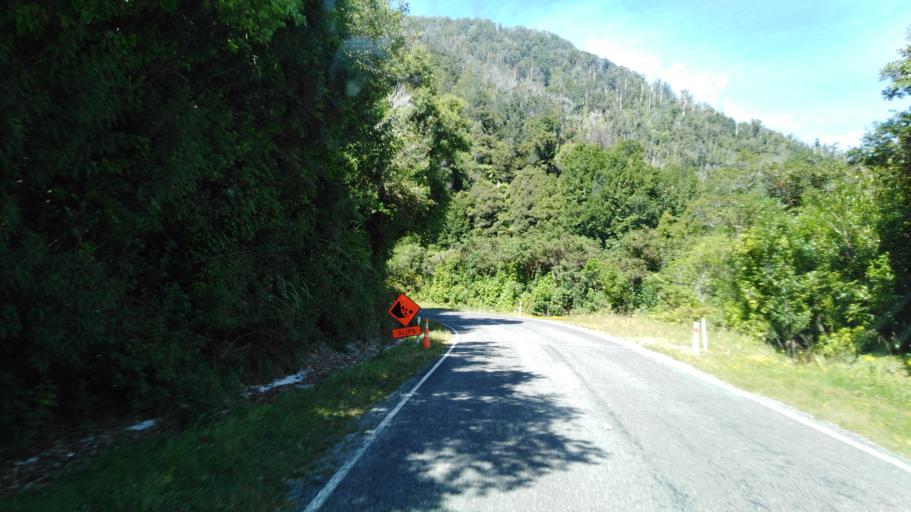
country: NZ
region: West Coast
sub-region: Buller District
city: Westport
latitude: -41.4921
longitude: 172.0495
